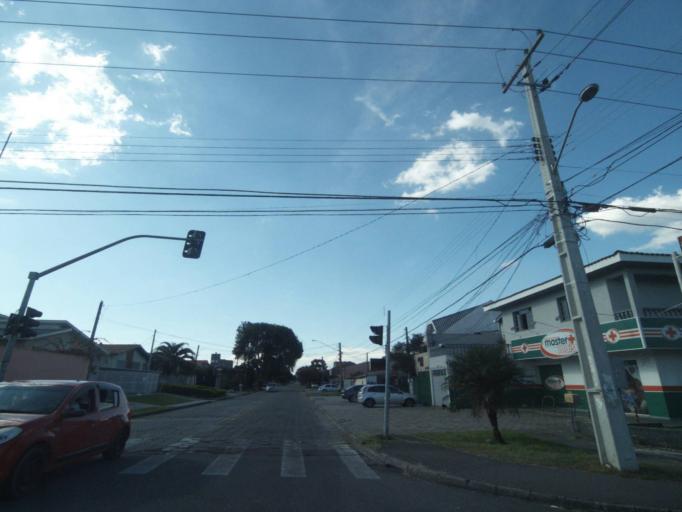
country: BR
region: Parana
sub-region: Pinhais
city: Pinhais
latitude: -25.4513
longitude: -49.2102
